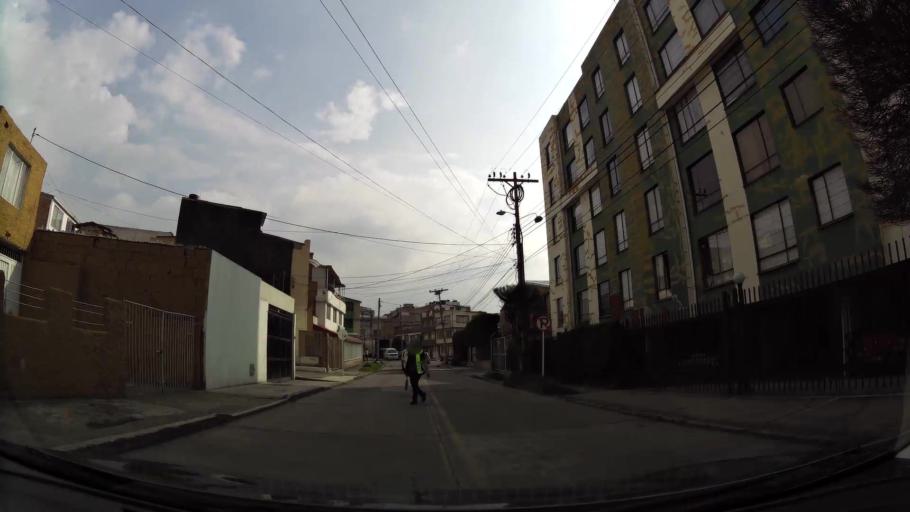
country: CO
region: Bogota D.C.
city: Barrio San Luis
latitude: 4.7240
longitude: -74.0577
